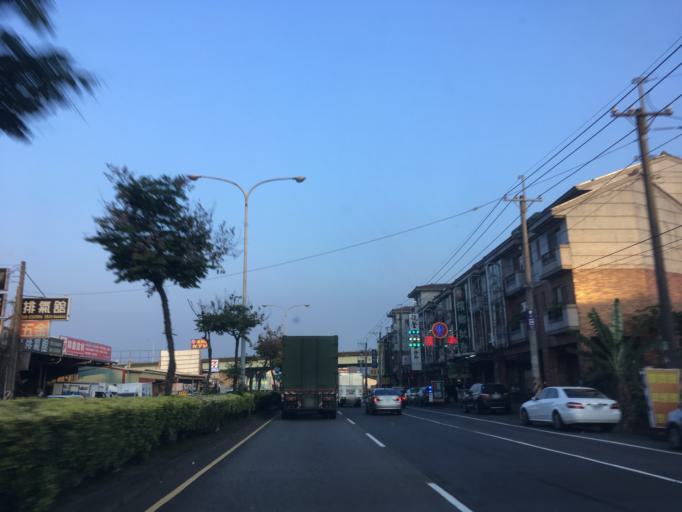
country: TW
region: Taiwan
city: Zhongxing New Village
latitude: 23.9993
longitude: 120.6596
